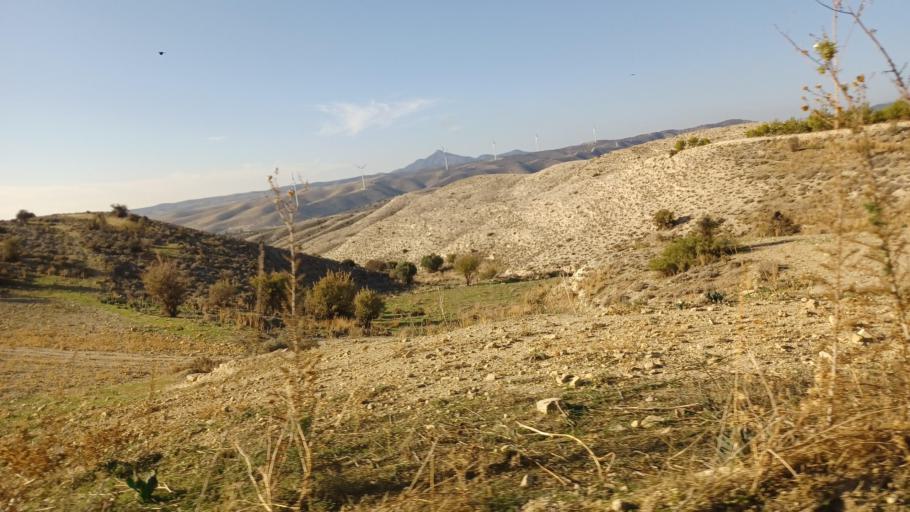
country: CY
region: Larnaka
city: Psevdas
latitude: 34.9501
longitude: 33.5123
